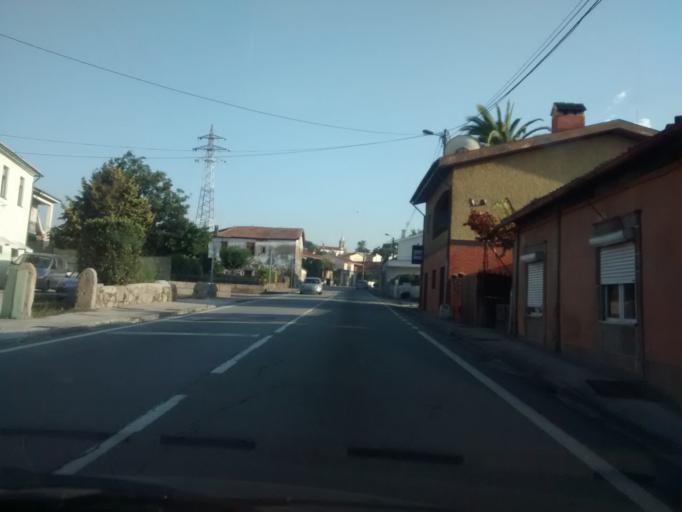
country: PT
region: Braga
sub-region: Braga
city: Adaufe
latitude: 41.5946
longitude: -8.4284
